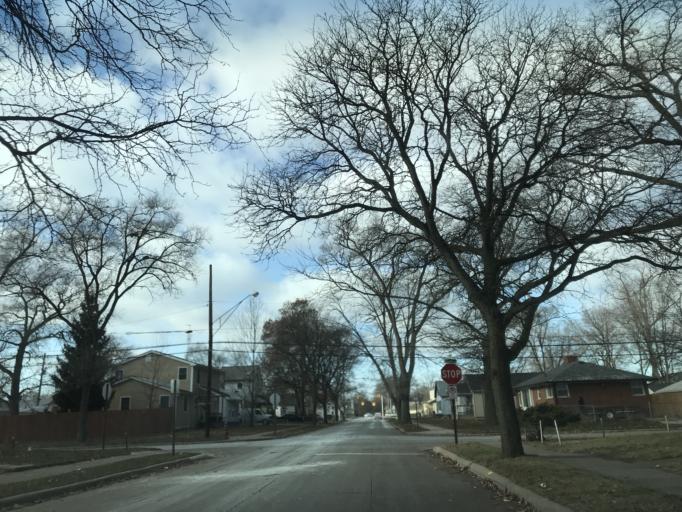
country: US
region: Michigan
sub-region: Oakland County
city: Hazel Park
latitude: 42.4549
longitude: -83.0930
